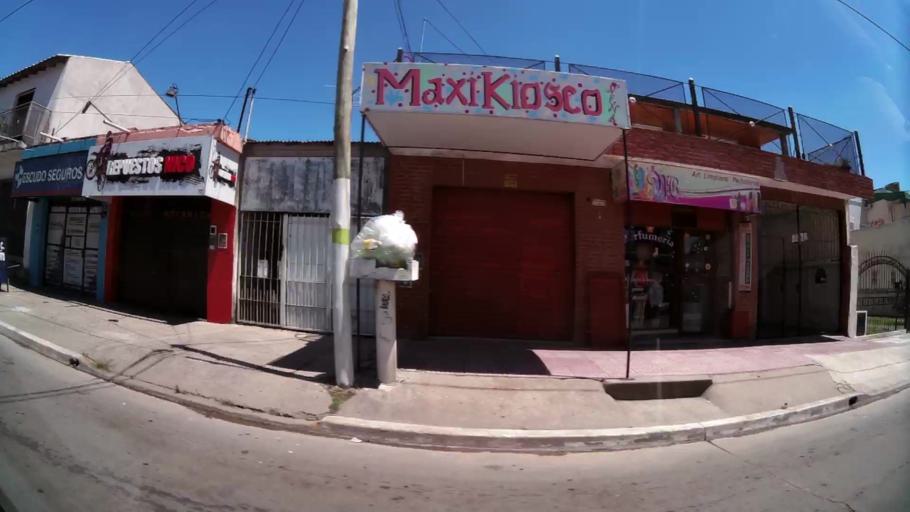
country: AR
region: Buenos Aires
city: Hurlingham
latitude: -34.5168
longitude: -58.6731
